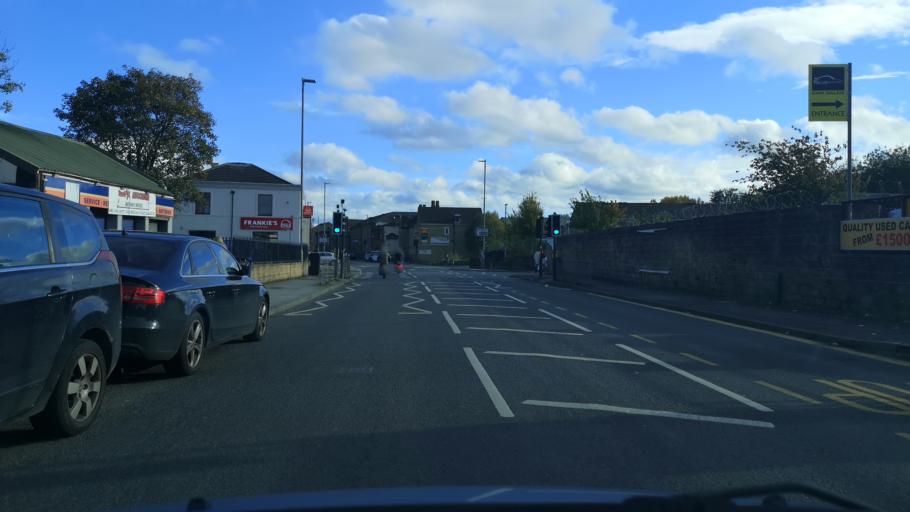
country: GB
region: England
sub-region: Kirklees
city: Batley
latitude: 53.7204
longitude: -1.6433
